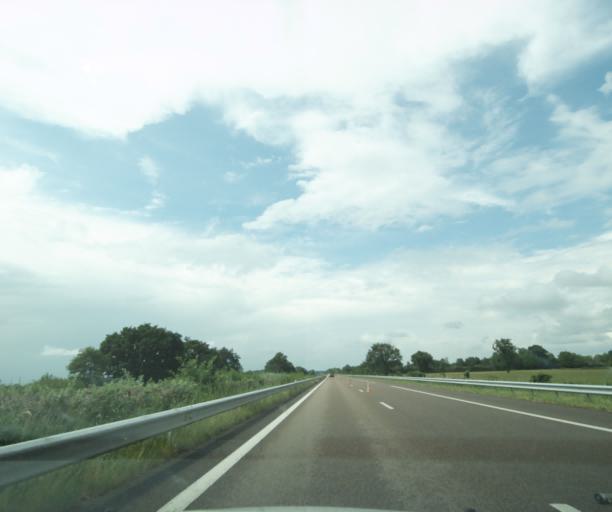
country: FR
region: Auvergne
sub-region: Departement de l'Allier
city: Estivareilles
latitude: 46.4589
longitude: 2.6840
